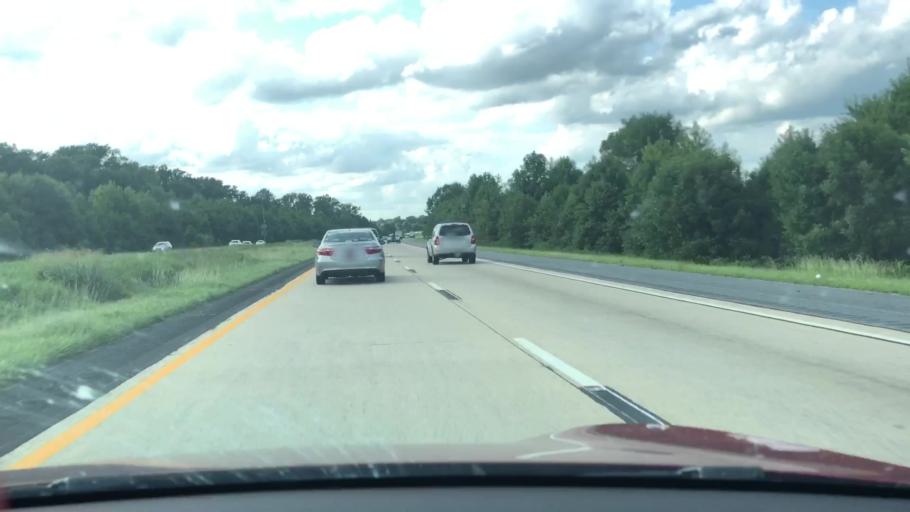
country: US
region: Delaware
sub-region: Kent County
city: Cheswold
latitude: 39.2292
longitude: -75.5744
